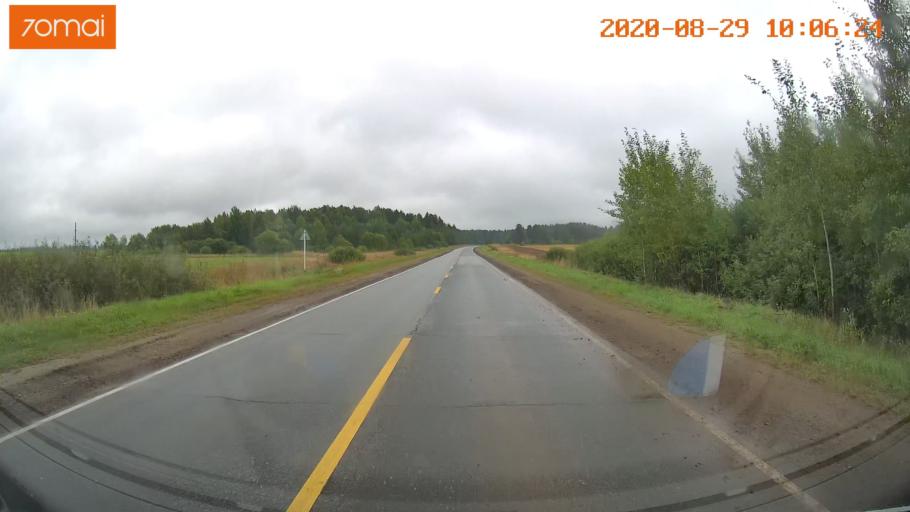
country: RU
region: Ivanovo
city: Kuznechikha
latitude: 57.3887
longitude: 42.5447
